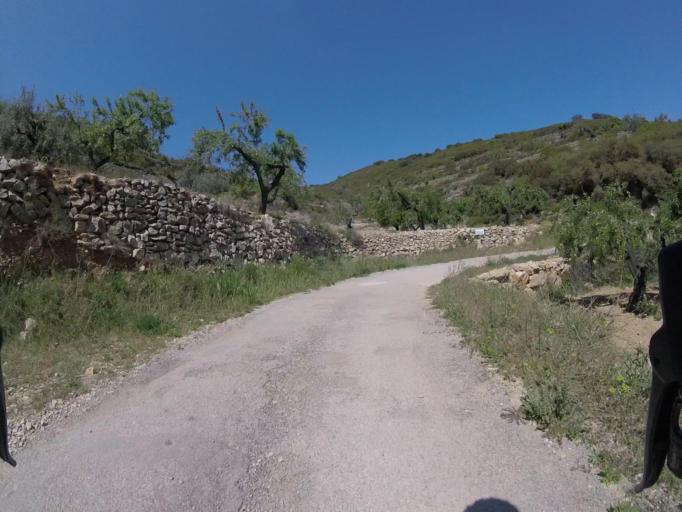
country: ES
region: Valencia
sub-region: Provincia de Castello
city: Sierra-Engarceran
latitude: 40.2549
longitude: -0.0260
